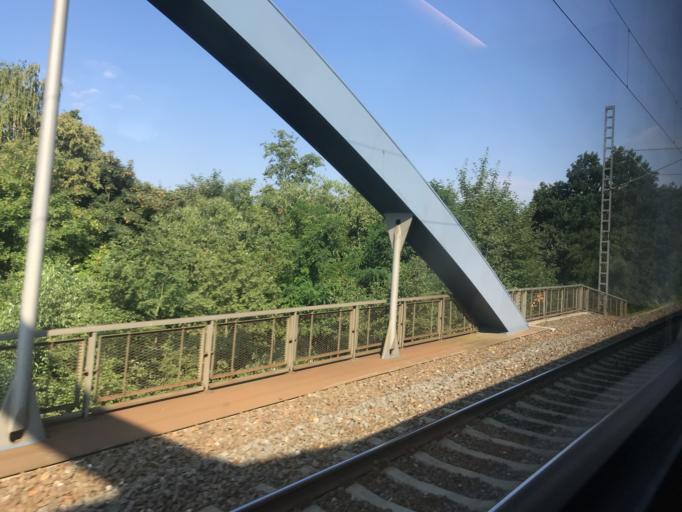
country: CZ
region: Jihocesky
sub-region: Okres Tabor
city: Sezimovo Usti
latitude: 49.3984
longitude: 14.6869
